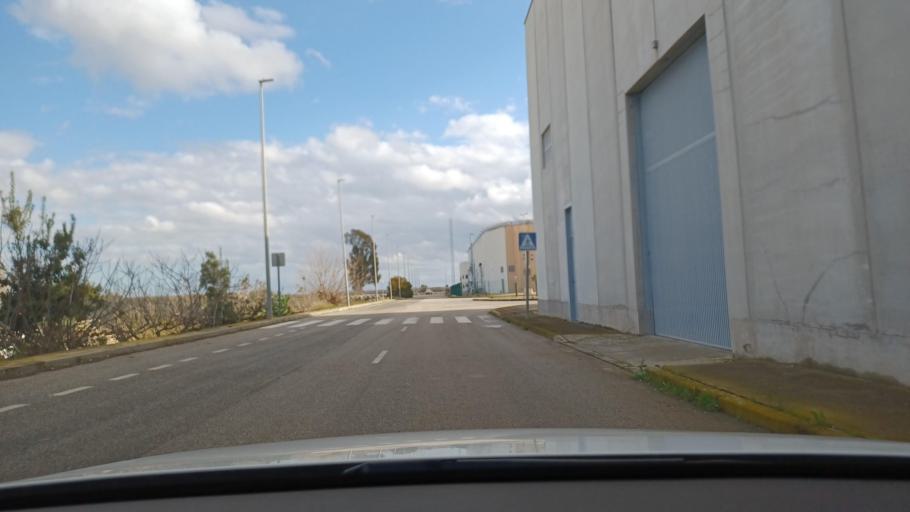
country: ES
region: Valencia
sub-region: Provincia de Alicante
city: Dolores
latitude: 38.1451
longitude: -0.7433
